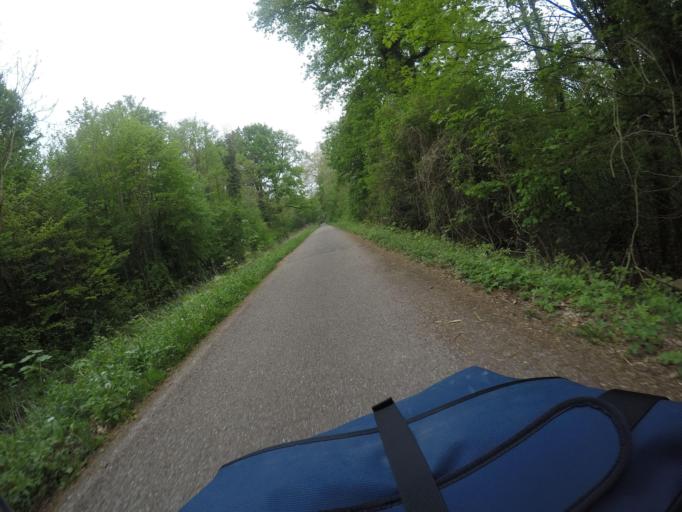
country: FR
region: Alsace
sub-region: Departement du Bas-Rhin
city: La Wantzenau
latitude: 48.6323
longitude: 7.8208
